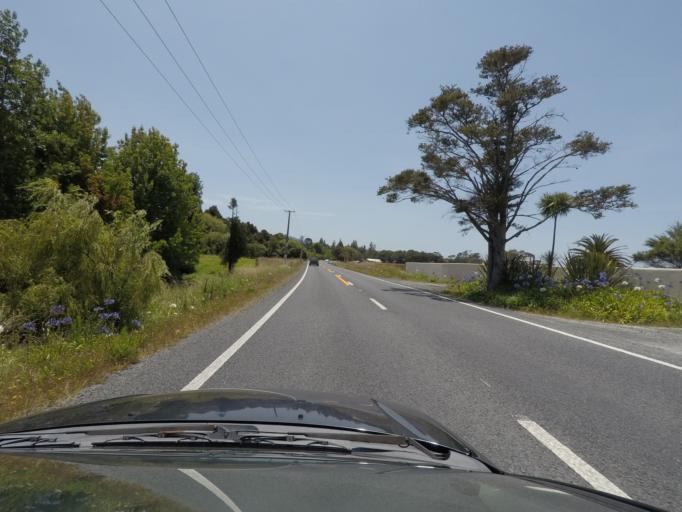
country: NZ
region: Auckland
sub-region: Auckland
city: Warkworth
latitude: -36.3716
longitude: 174.6808
